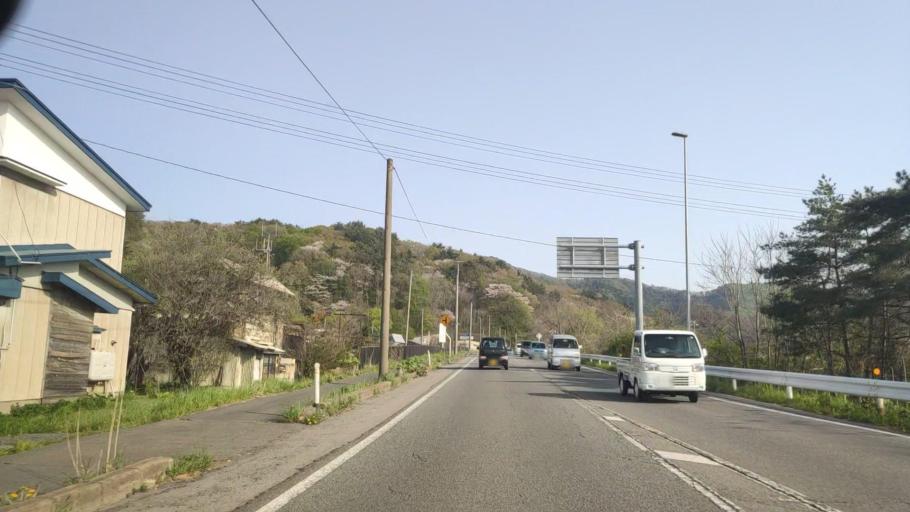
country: JP
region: Aomori
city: Aomori Shi
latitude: 40.8771
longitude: 140.8503
